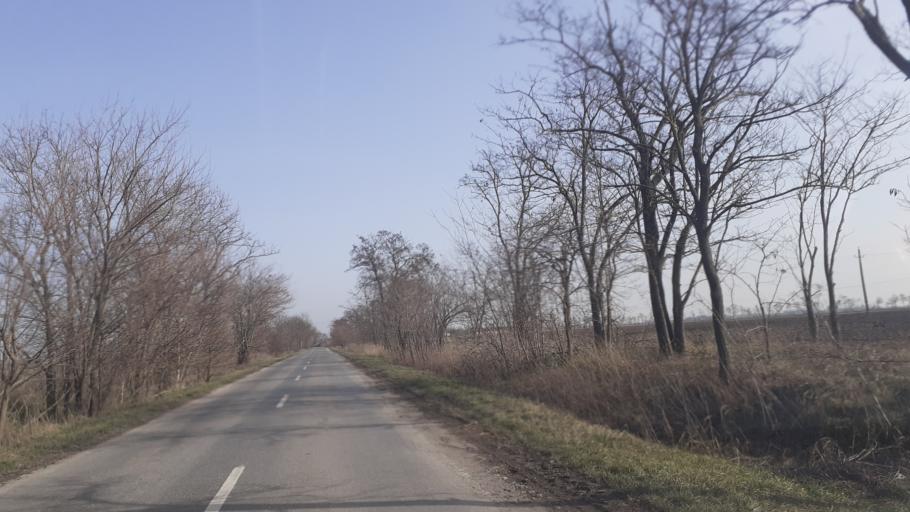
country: HU
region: Bacs-Kiskun
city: Tass
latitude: 47.0203
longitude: 18.9999
